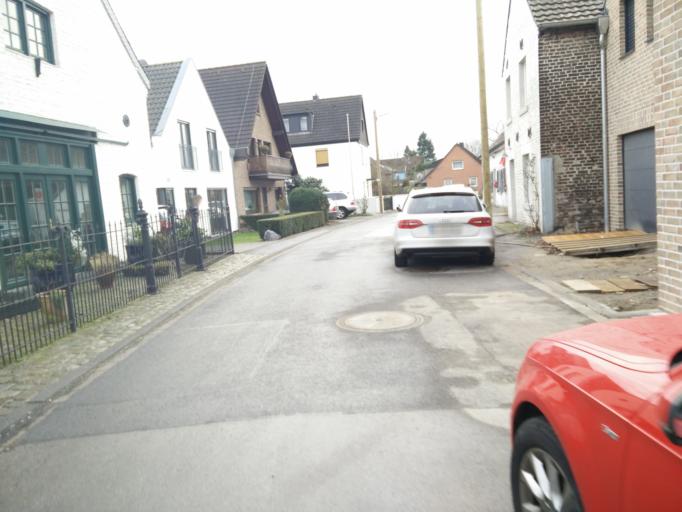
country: DE
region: North Rhine-Westphalia
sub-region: Regierungsbezirk Dusseldorf
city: Dusseldorf
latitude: 51.3088
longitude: 6.7596
